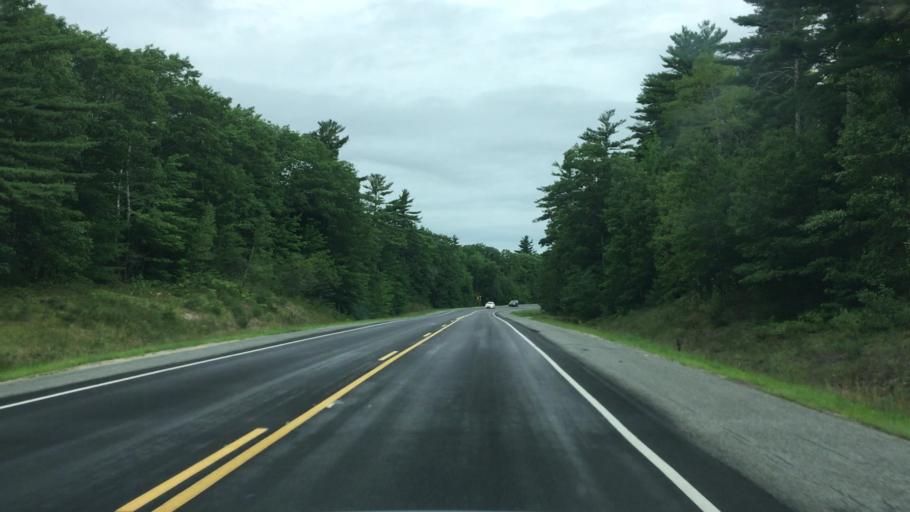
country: US
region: Maine
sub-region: Washington County
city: Cherryfield
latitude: 44.9053
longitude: -67.8567
